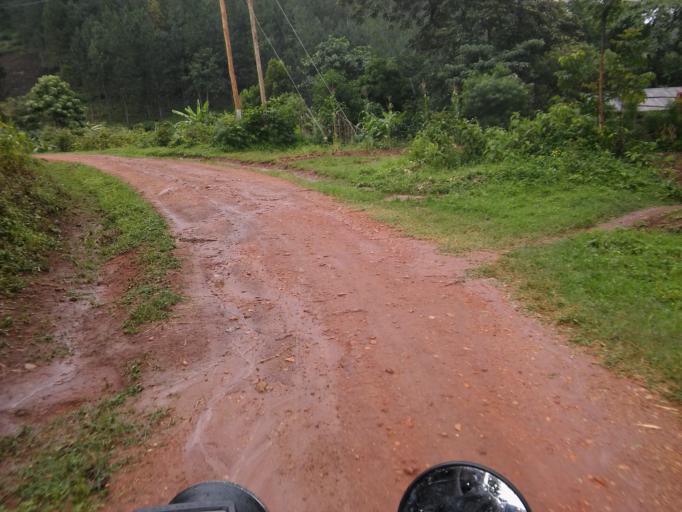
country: UG
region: Eastern Region
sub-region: Bududa District
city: Bududa
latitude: 0.9966
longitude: 34.2375
